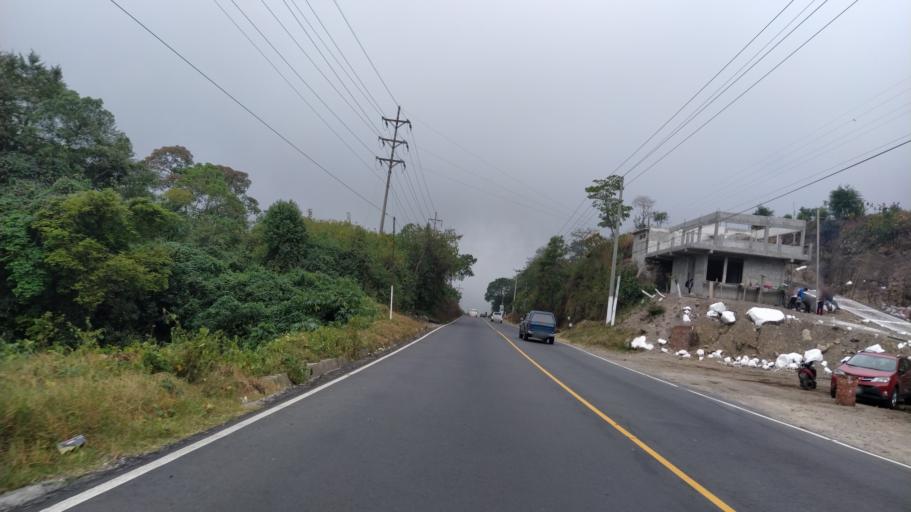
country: GT
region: Quetzaltenango
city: Zunil
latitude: 14.7371
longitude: -91.5210
